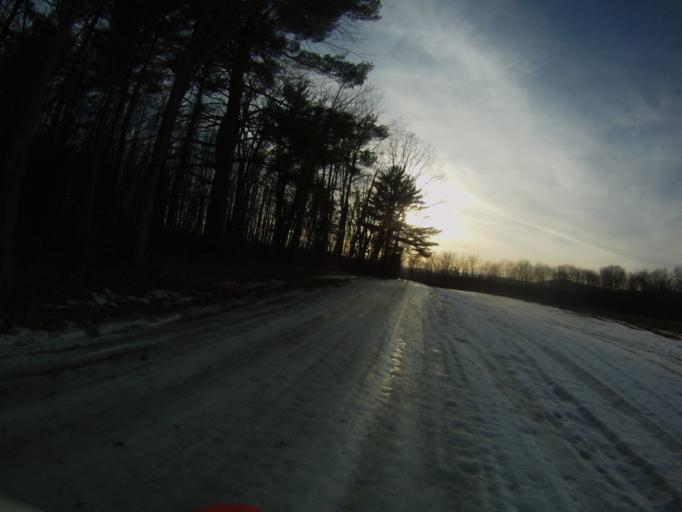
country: US
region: New York
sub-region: Essex County
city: Port Henry
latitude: 44.0534
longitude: -73.3919
